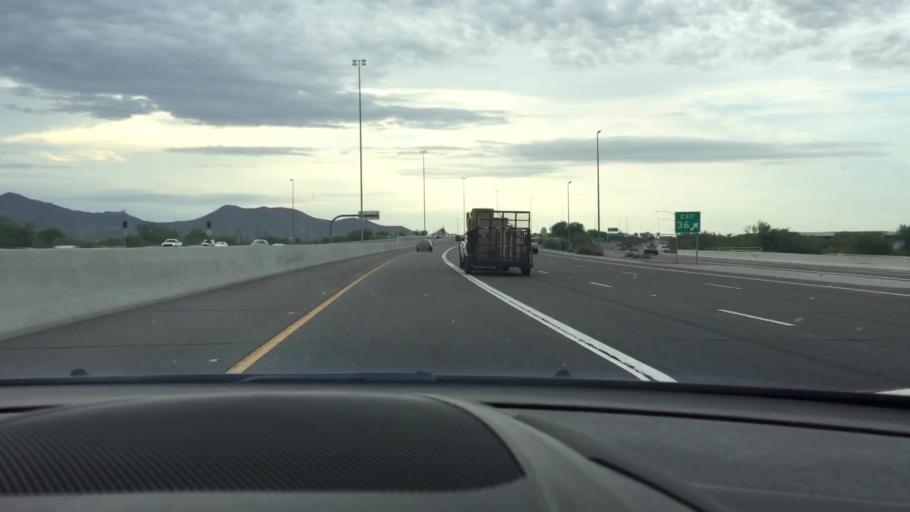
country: US
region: Arizona
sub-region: Maricopa County
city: Paradise Valley
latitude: 33.6523
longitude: -111.8973
